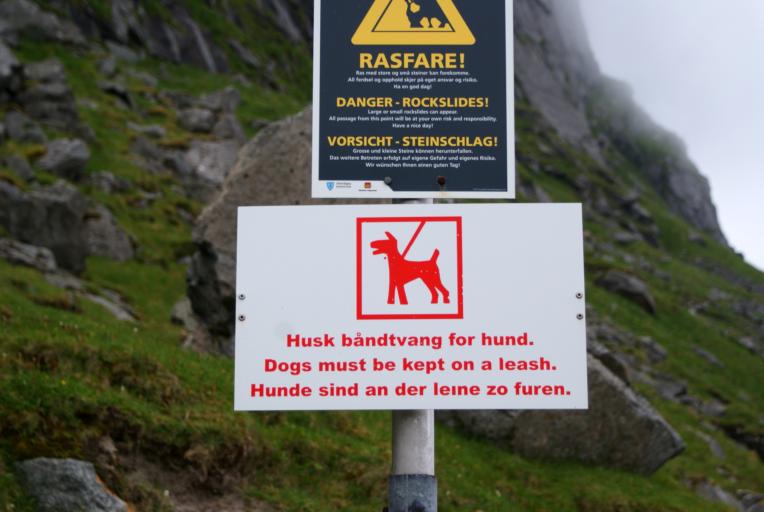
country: NO
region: Nordland
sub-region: Vestvagoy
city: Gravdal
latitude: 68.2095
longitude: 13.5017
